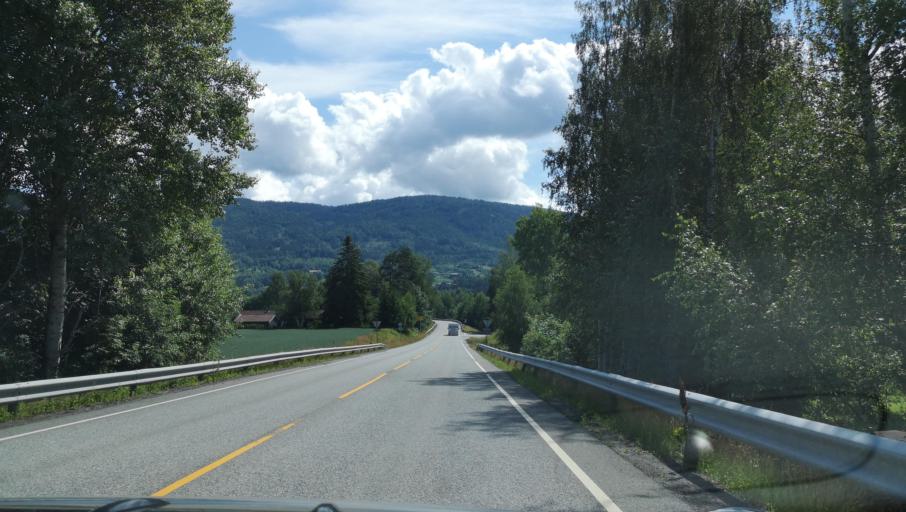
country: NO
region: Buskerud
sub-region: Modum
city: Vikersund
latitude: 59.9647
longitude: 9.9835
